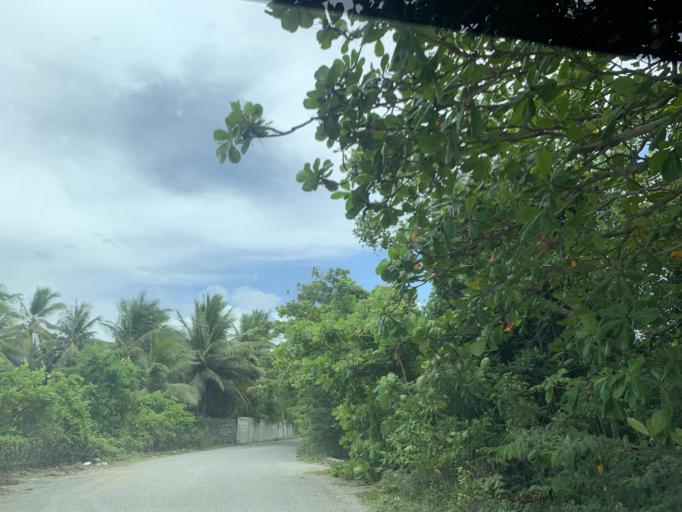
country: DO
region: Puerto Plata
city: Imbert
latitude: 19.8273
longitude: -70.7780
